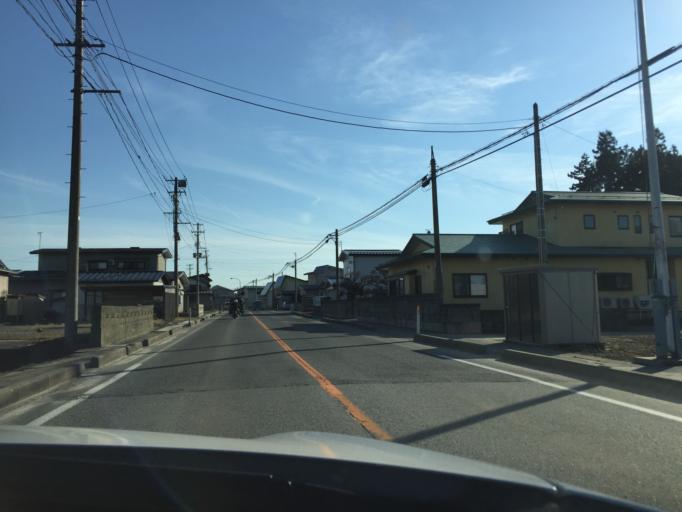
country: JP
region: Yamagata
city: Nagai
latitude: 38.0869
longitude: 140.0423
